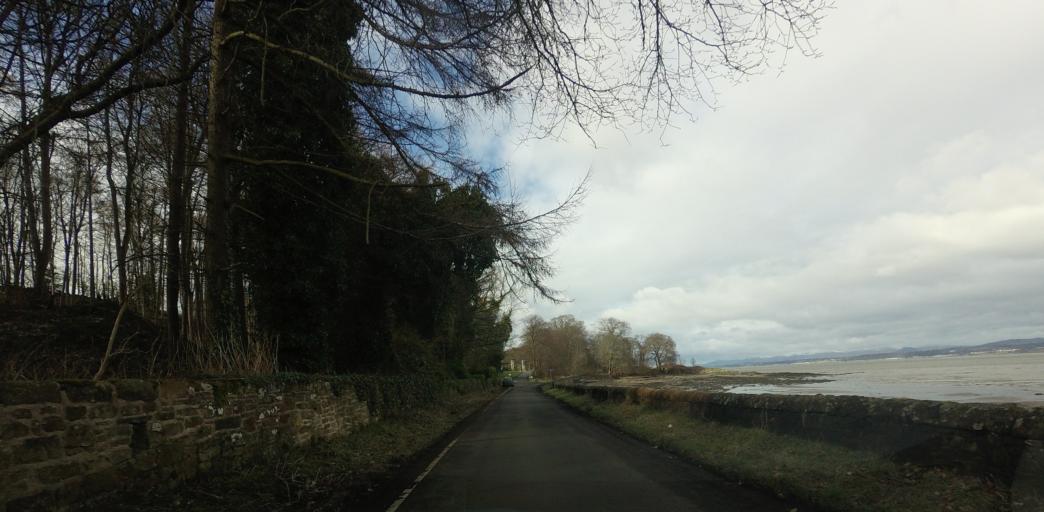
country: GB
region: Scotland
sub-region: Edinburgh
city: Queensferry
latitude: 55.9941
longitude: -3.4399
